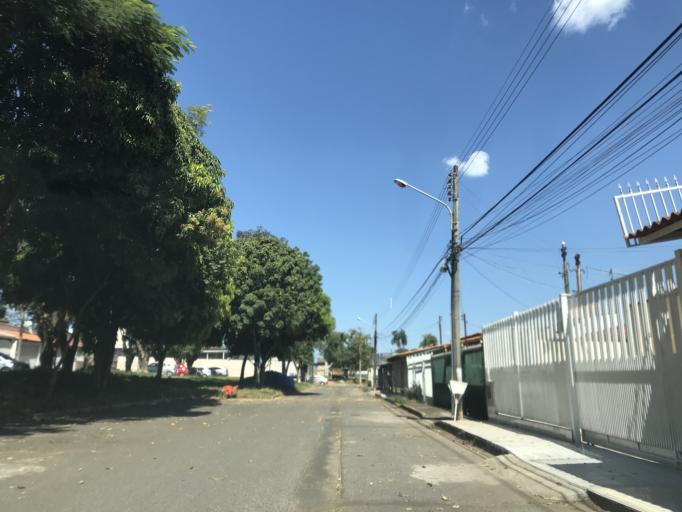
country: BR
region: Federal District
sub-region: Brasilia
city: Brasilia
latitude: -15.6589
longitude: -47.8081
